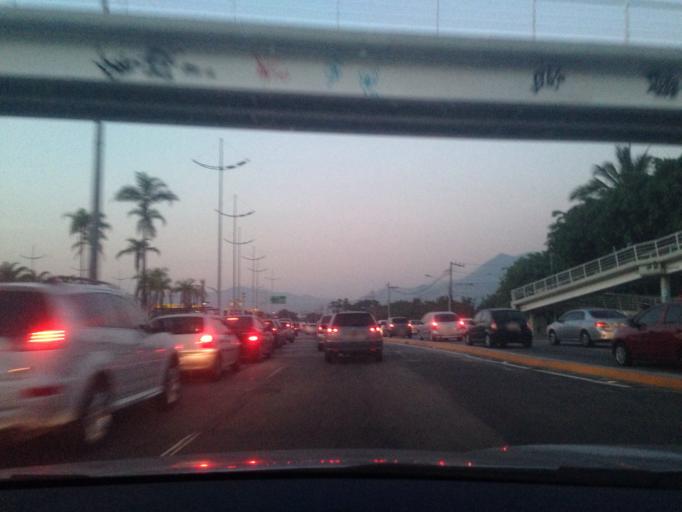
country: BR
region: Rio de Janeiro
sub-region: Sao Joao De Meriti
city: Sao Joao de Meriti
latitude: -22.9710
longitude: -43.3608
